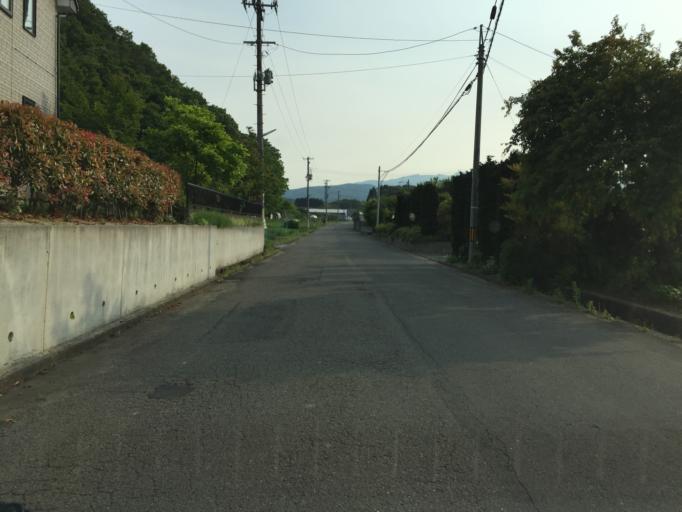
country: JP
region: Fukushima
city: Fukushima-shi
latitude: 37.7287
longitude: 140.4338
